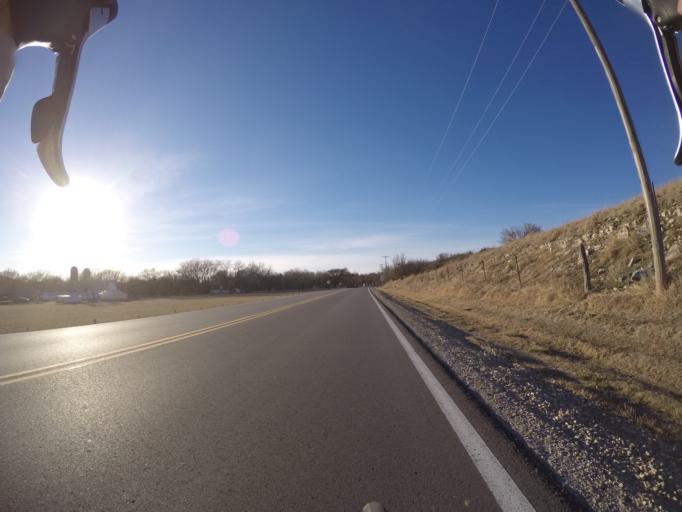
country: US
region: Kansas
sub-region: Riley County
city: Ogden
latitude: 39.2222
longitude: -96.7040
